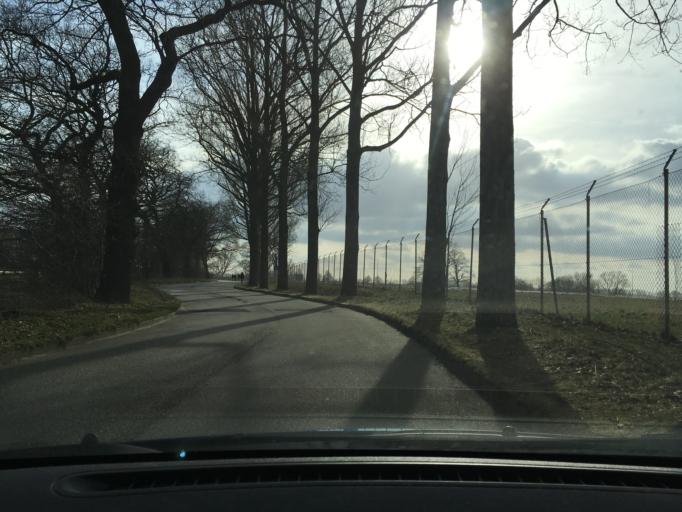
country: DE
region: Schleswig-Holstein
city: Wedel
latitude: 53.5688
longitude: 9.7347
